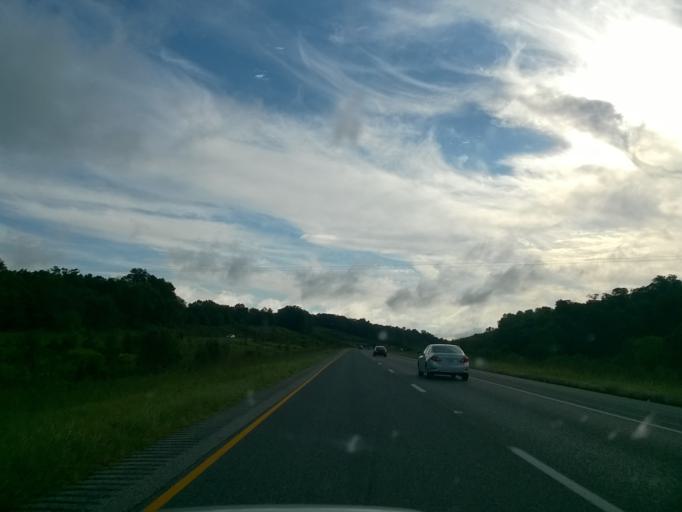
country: US
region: Indiana
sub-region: Dubois County
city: Ferdinand
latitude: 38.2070
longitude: -86.7976
